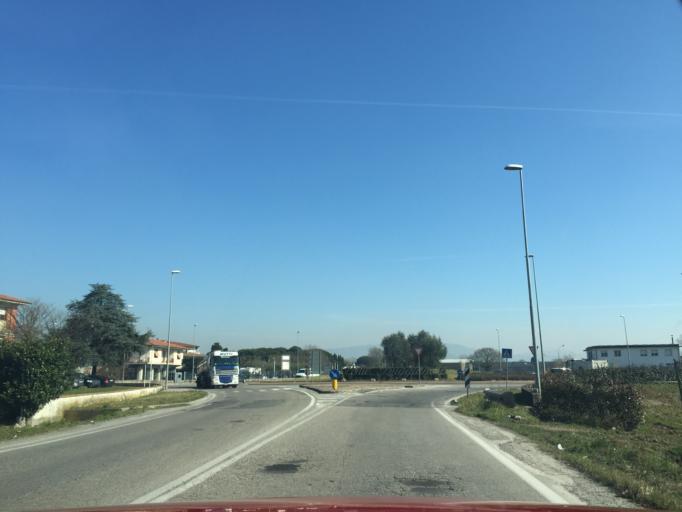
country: IT
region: Tuscany
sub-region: Provincia di Pistoia
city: Ponte Buggianese
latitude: 43.8527
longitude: 10.7457
